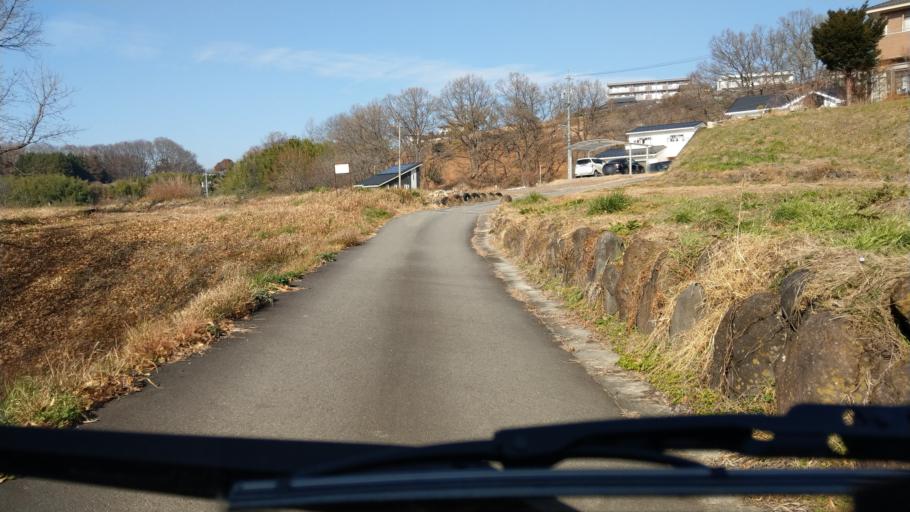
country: JP
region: Nagano
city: Komoro
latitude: 36.3200
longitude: 138.4247
